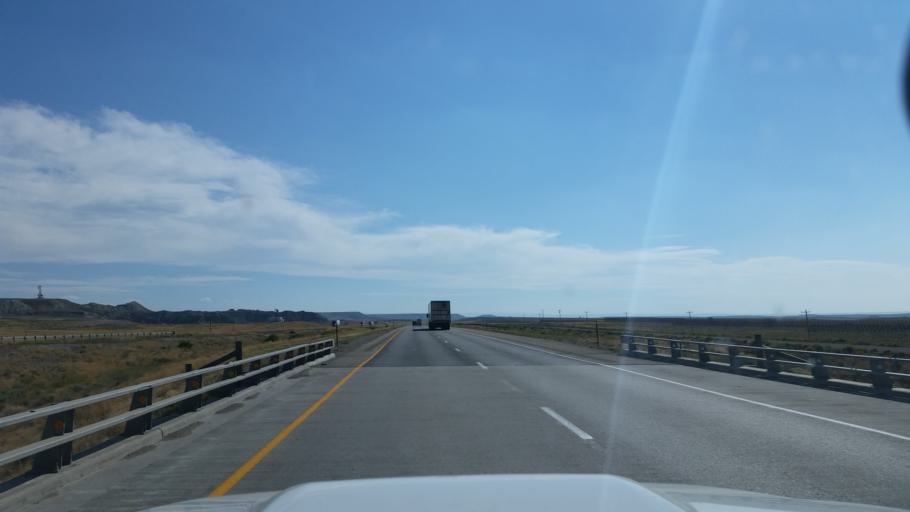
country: US
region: Wyoming
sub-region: Uinta County
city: Lyman
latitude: 41.4839
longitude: -110.0250
